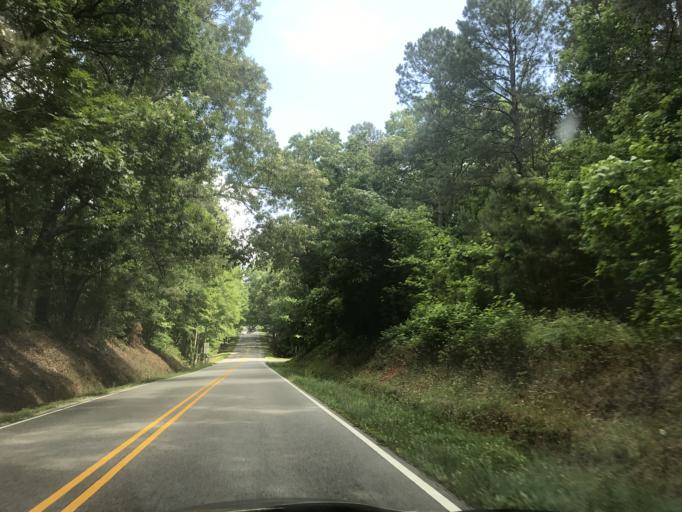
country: US
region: North Carolina
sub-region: Nash County
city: Spring Hope
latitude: 35.9262
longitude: -78.1922
